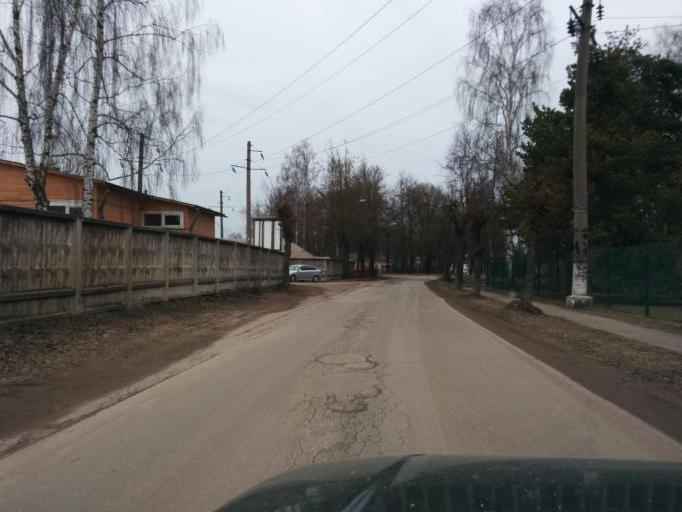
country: LV
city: Tireli
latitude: 56.9473
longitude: 23.6317
